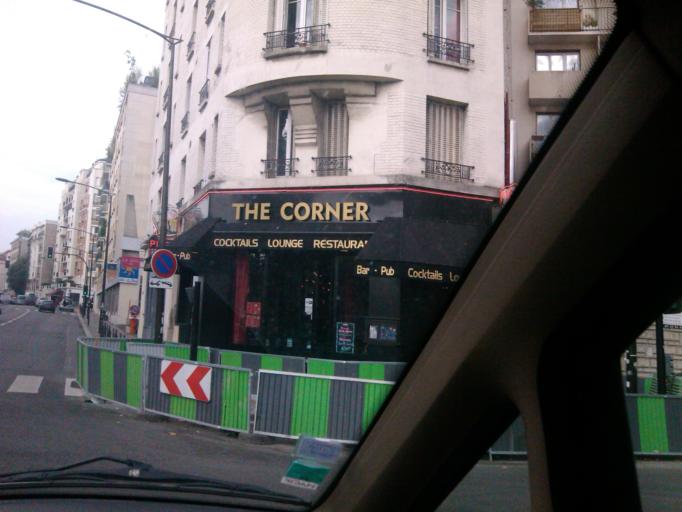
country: FR
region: Ile-de-France
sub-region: Departement des Hauts-de-Seine
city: Boulogne-Billancourt
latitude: 48.8320
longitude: 2.2536
